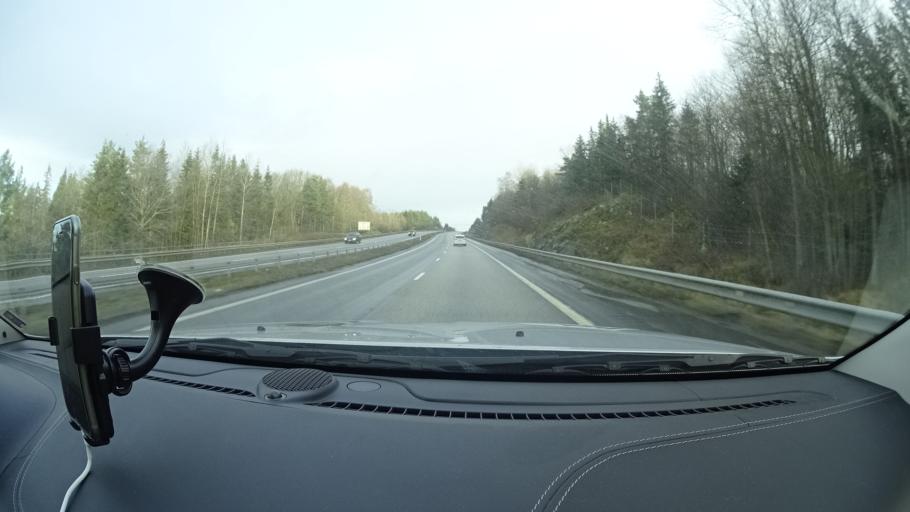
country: SE
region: Joenkoeping
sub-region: Jonkopings Kommun
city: Kaxholmen
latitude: 57.9476
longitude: 14.3425
